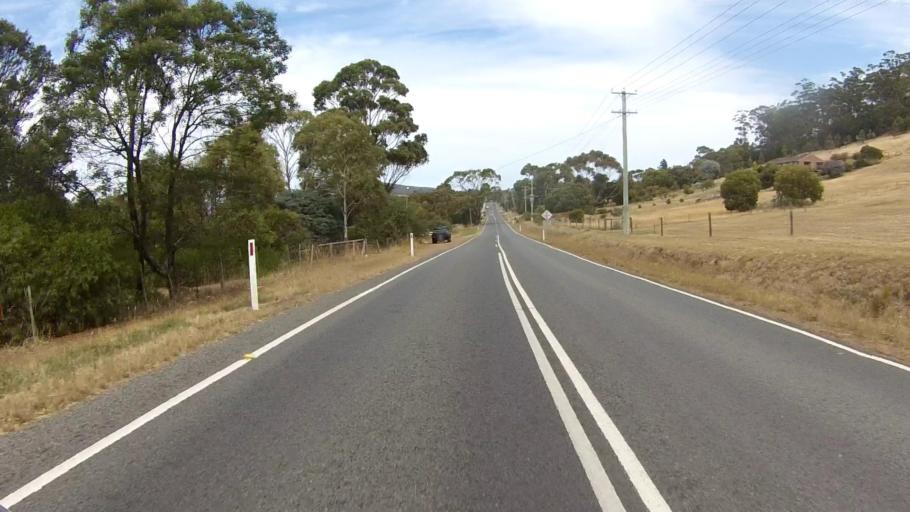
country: AU
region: Tasmania
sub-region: Clarence
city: Lauderdale
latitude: -42.9000
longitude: 147.4798
